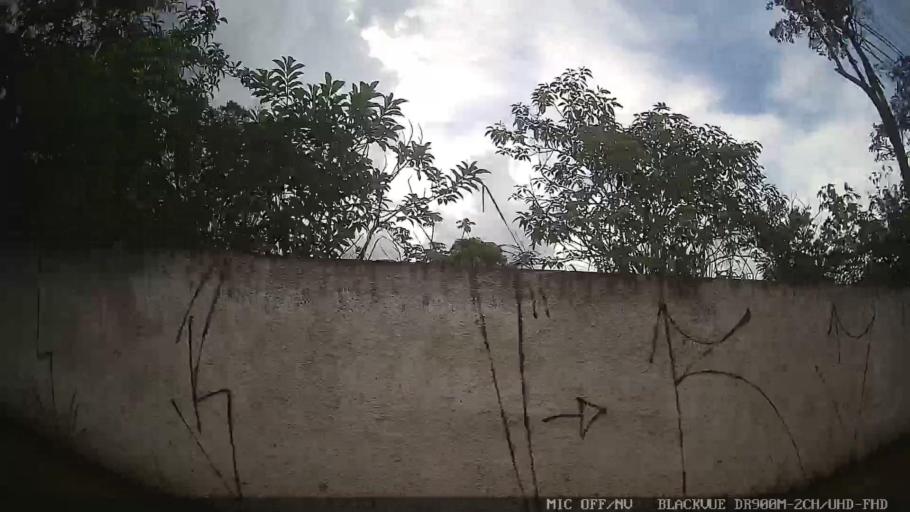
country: BR
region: Sao Paulo
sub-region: Itaquaquecetuba
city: Itaquaquecetuba
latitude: -23.4855
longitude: -46.3058
